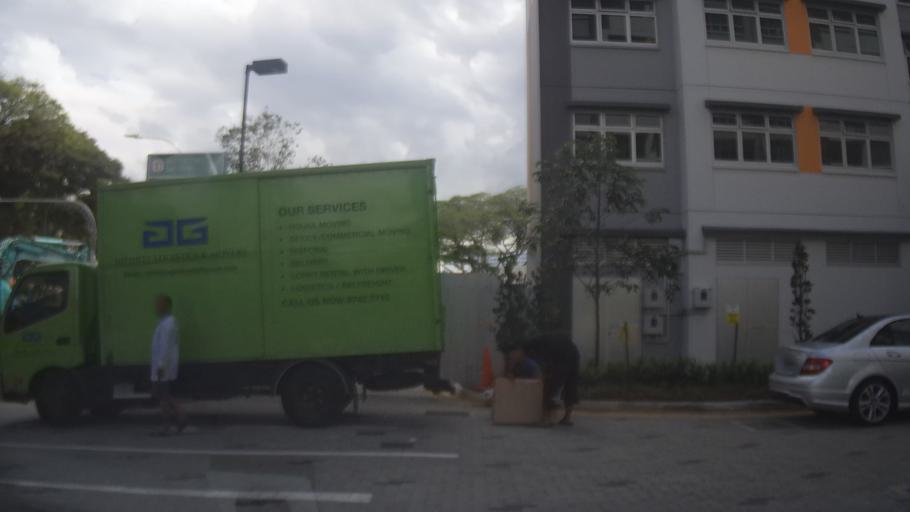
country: SG
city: Singapore
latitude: 1.3239
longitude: 103.8891
